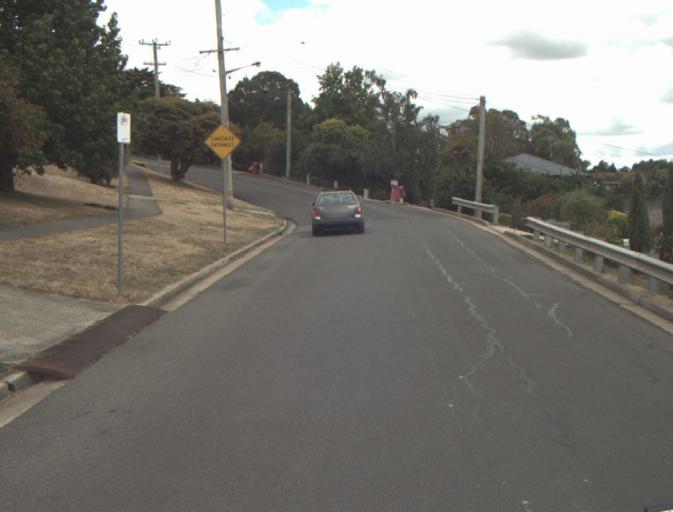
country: AU
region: Tasmania
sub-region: Launceston
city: Summerhill
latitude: -41.4642
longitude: 147.1396
